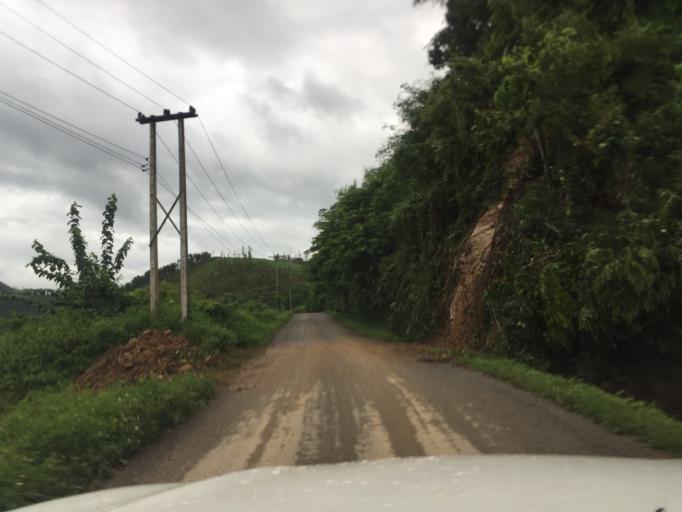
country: LA
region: Oudomxai
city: Muang La
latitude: 20.9724
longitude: 102.2225
